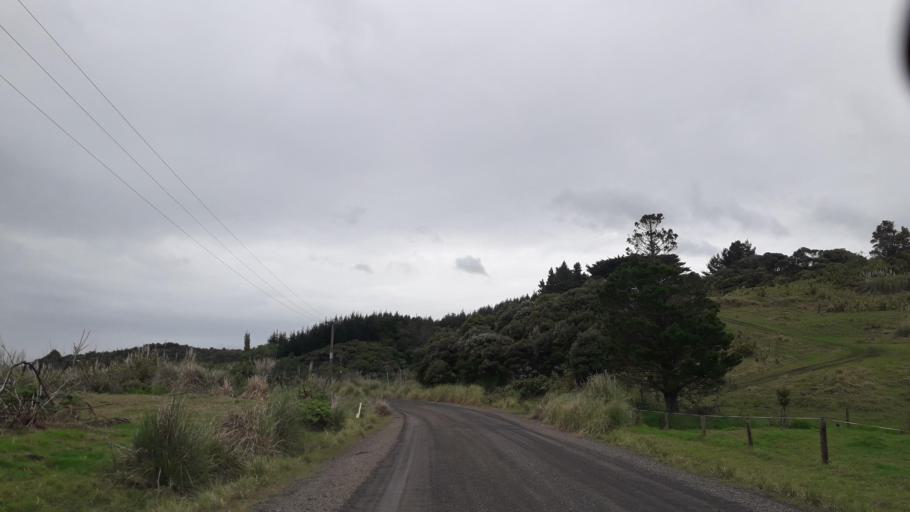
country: NZ
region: Northland
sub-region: Far North District
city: Kaitaia
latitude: -35.4062
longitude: 173.3789
